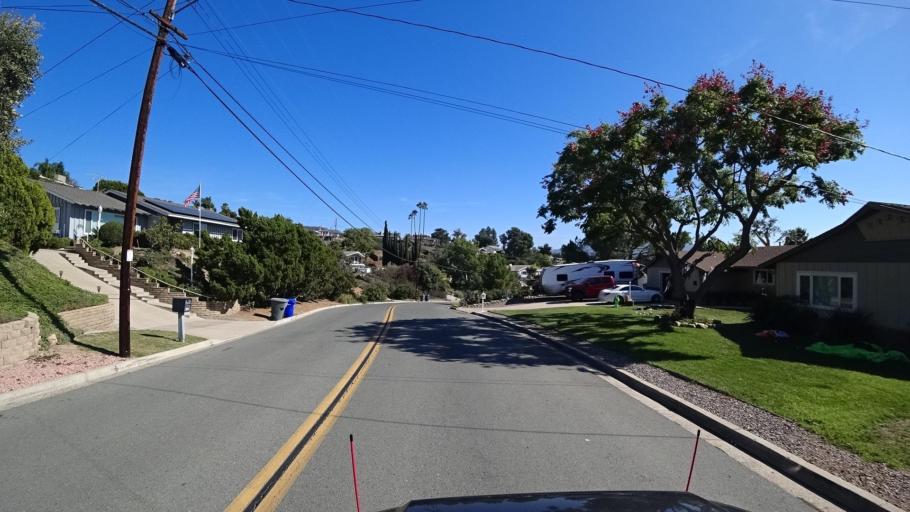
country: US
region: California
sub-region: San Diego County
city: Casa de Oro-Mount Helix
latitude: 32.7546
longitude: -116.9785
